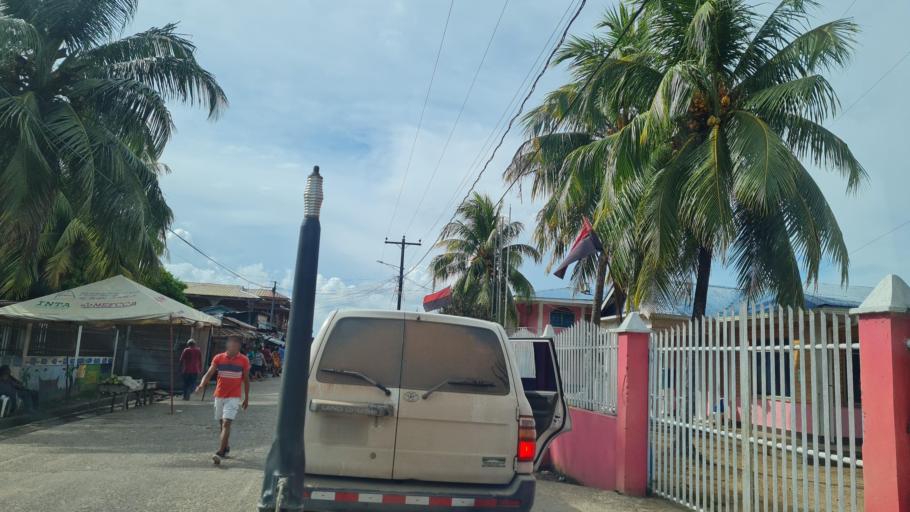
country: NI
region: Atlantico Norte (RAAN)
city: Waspam
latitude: 14.7422
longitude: -83.9713
